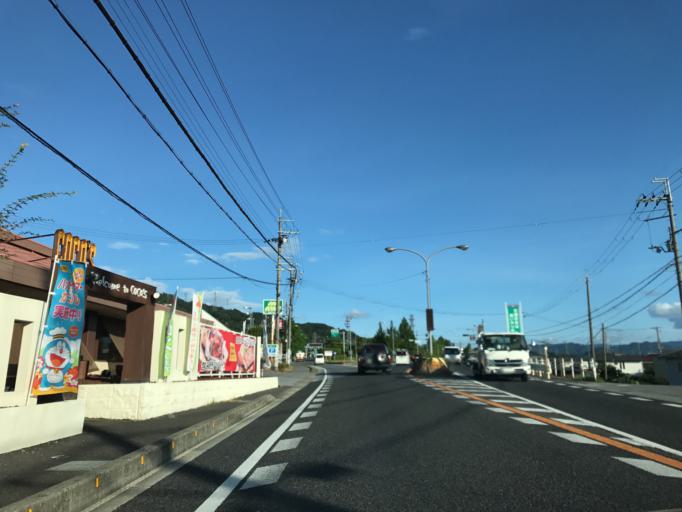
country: JP
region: Shiga Prefecture
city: Hikone
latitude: 35.2630
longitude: 136.2710
